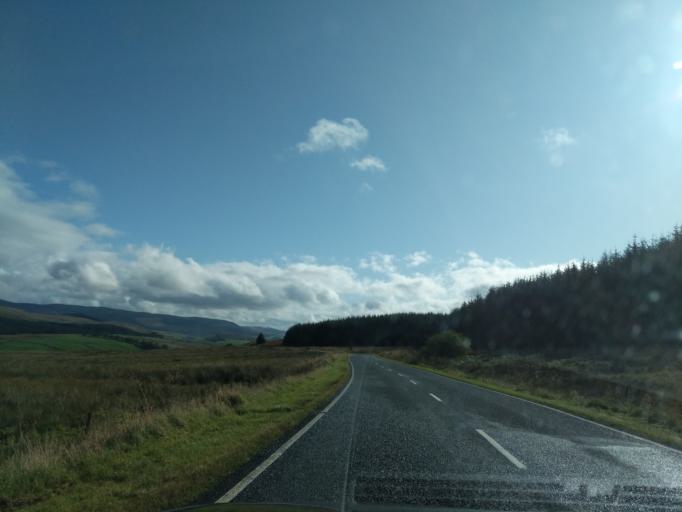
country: GB
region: Scotland
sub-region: Dumfries and Galloway
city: Moffat
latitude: 55.3807
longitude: -3.4822
